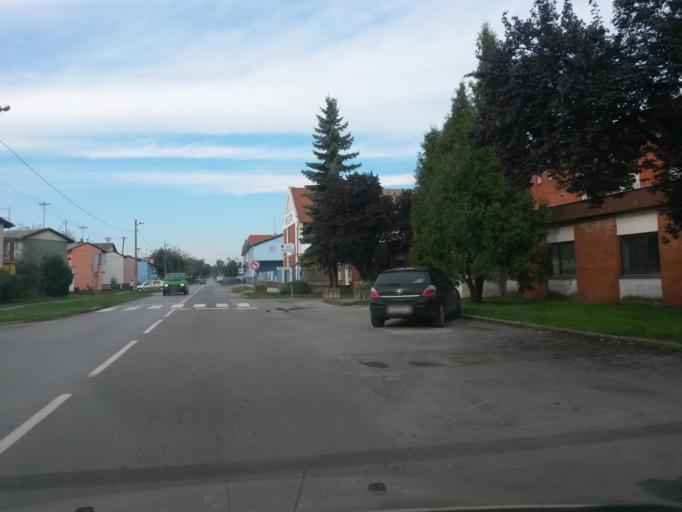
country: HR
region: Osjecko-Baranjska
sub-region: Grad Osijek
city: Osijek
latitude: 45.5540
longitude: 18.7312
